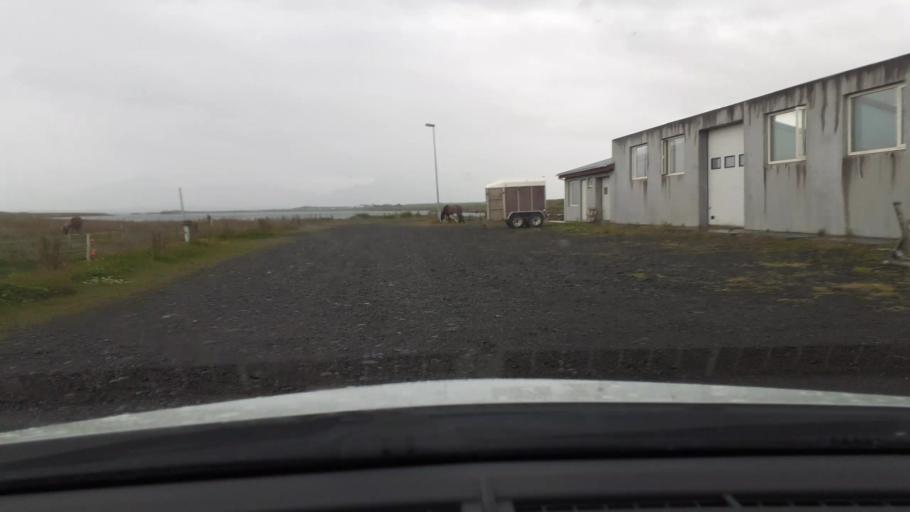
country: IS
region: West
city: Akranes
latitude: 64.3422
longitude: -22.0210
